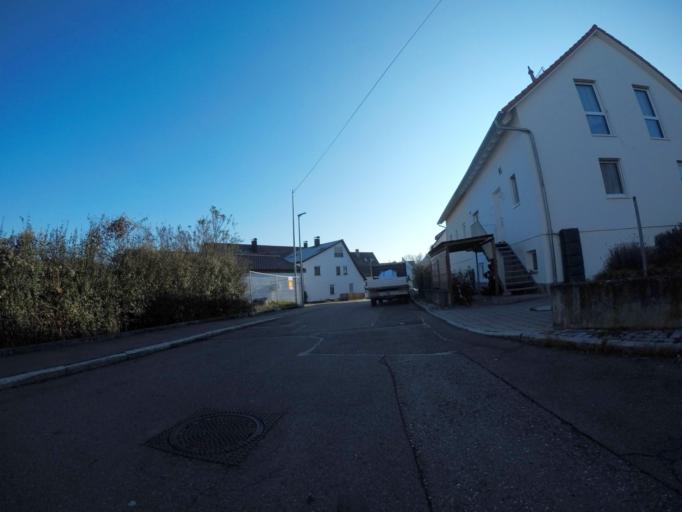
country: DE
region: Baden-Wuerttemberg
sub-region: Tuebingen Region
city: Reutlingen
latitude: 48.5238
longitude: 9.2254
